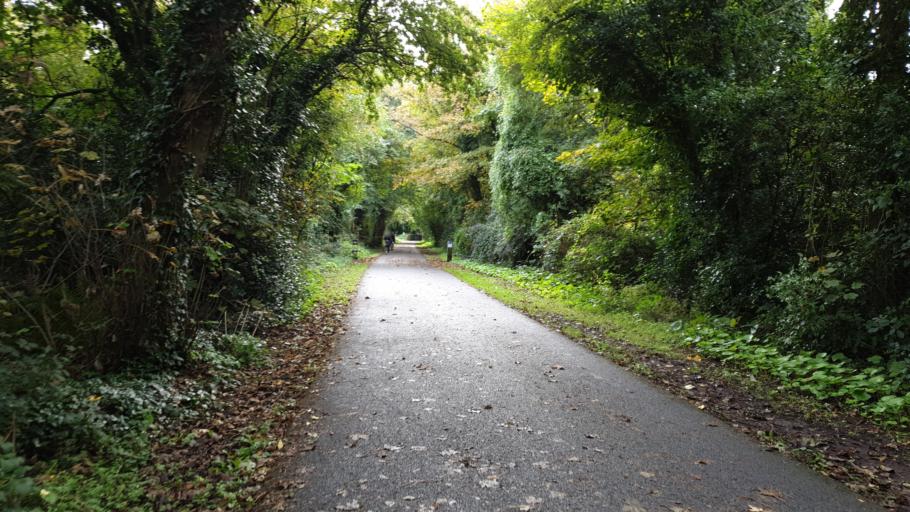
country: IE
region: Munster
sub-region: County Cork
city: Cork
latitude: 51.8985
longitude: -8.4232
